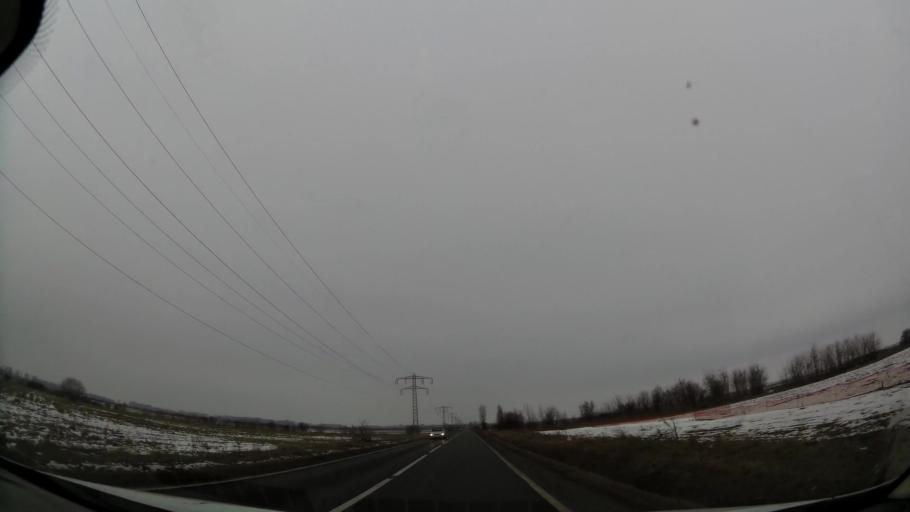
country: RO
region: Dambovita
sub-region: Comuna Contesti
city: Balteni
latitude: 44.6618
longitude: 25.6731
